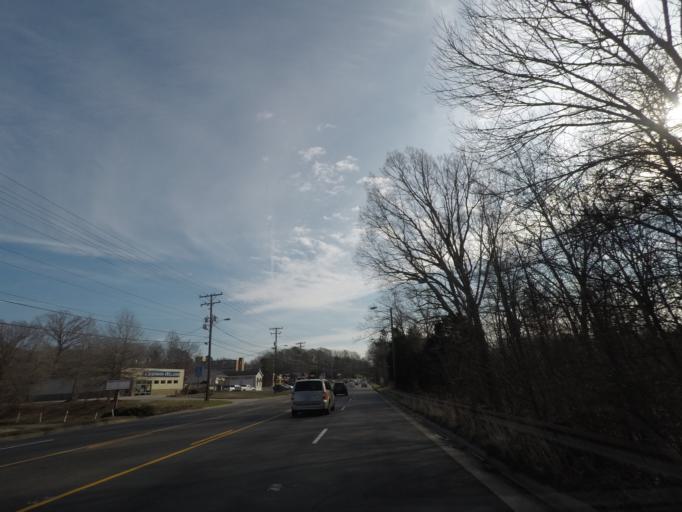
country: US
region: North Carolina
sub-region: Durham County
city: Durham
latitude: 36.0669
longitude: -78.9066
